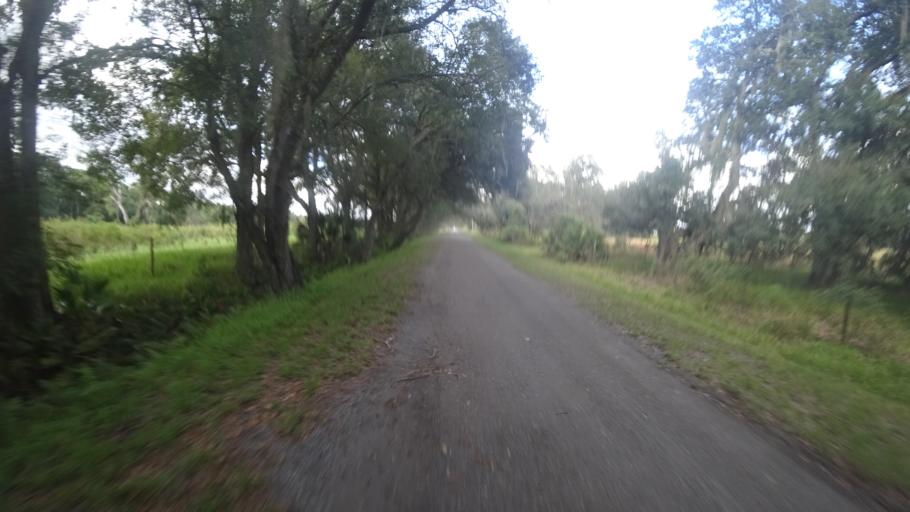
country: US
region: Florida
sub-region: Hillsborough County
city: Wimauma
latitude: 27.5372
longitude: -82.1747
